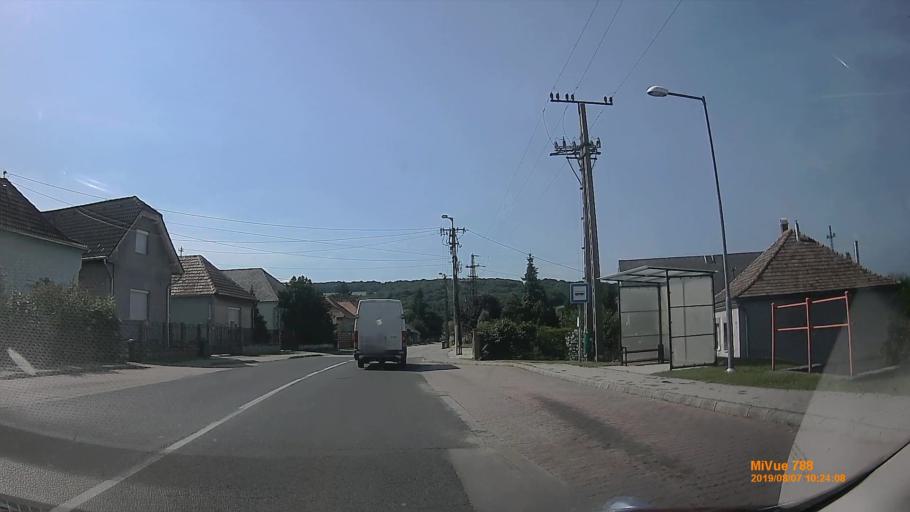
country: HU
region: Veszprem
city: Ajka
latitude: 47.0924
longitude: 17.5642
